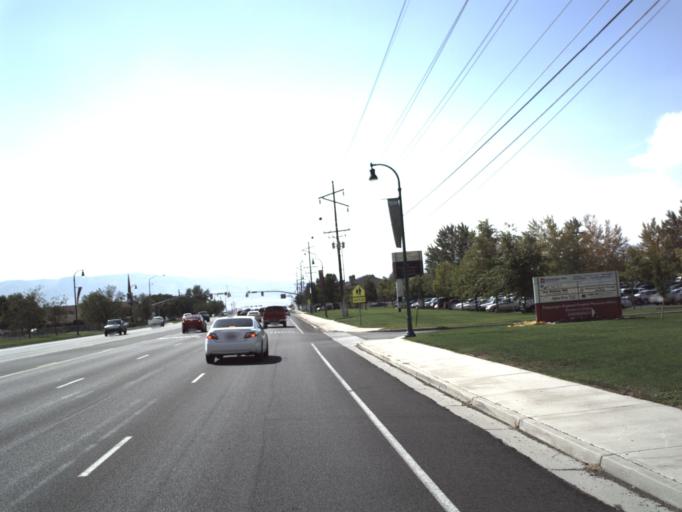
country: US
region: Utah
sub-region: Utah County
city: Orem
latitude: 40.3122
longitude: -111.7093
